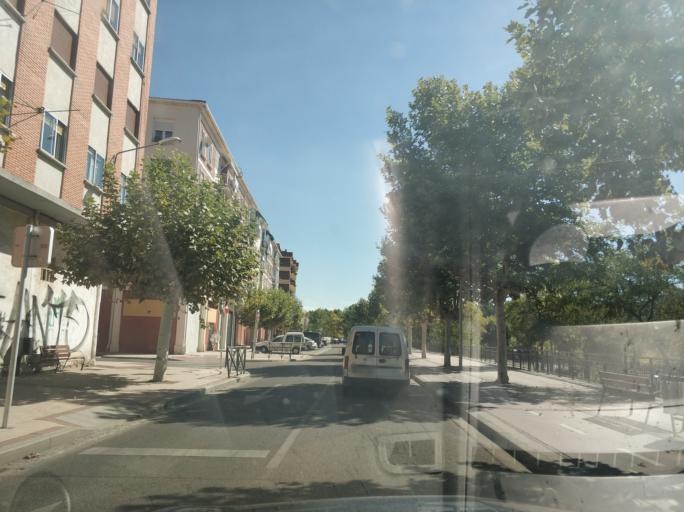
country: ES
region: Castille and Leon
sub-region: Provincia de Burgos
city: Aranda de Duero
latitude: 41.6691
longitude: -3.6804
